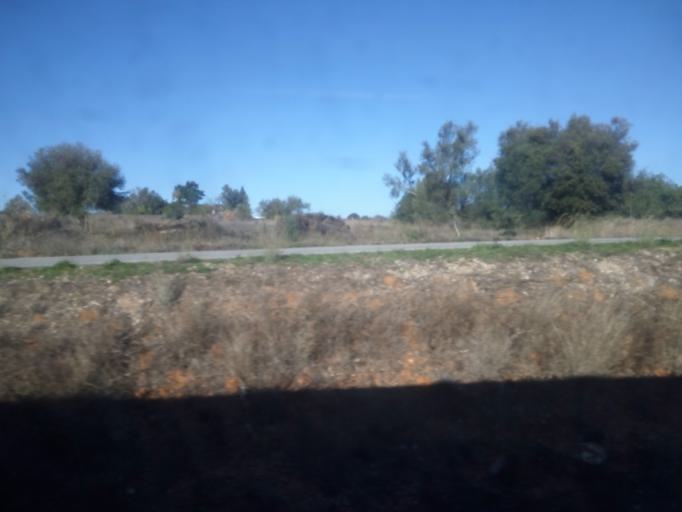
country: PT
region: Faro
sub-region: Loule
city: Boliqueime
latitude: 37.1139
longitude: -8.1847
